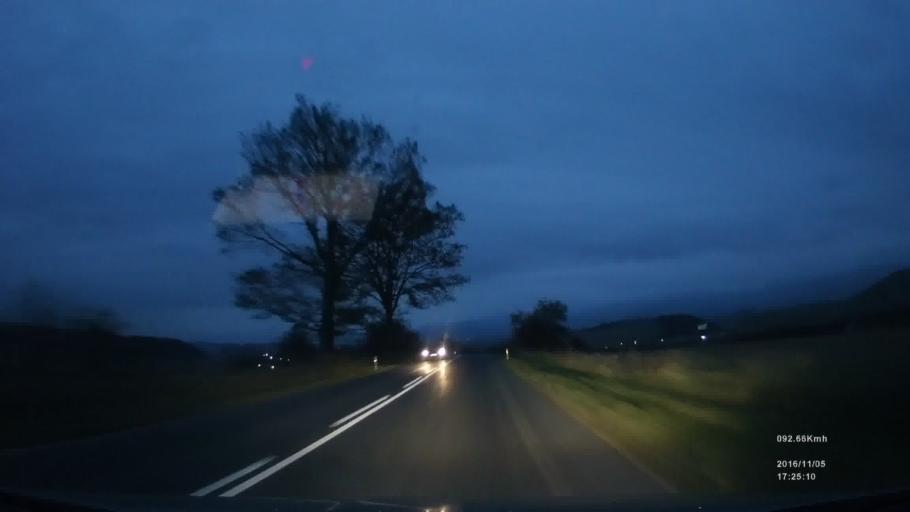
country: SK
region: Presovsky
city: Lubica
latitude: 49.0249
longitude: 20.4395
